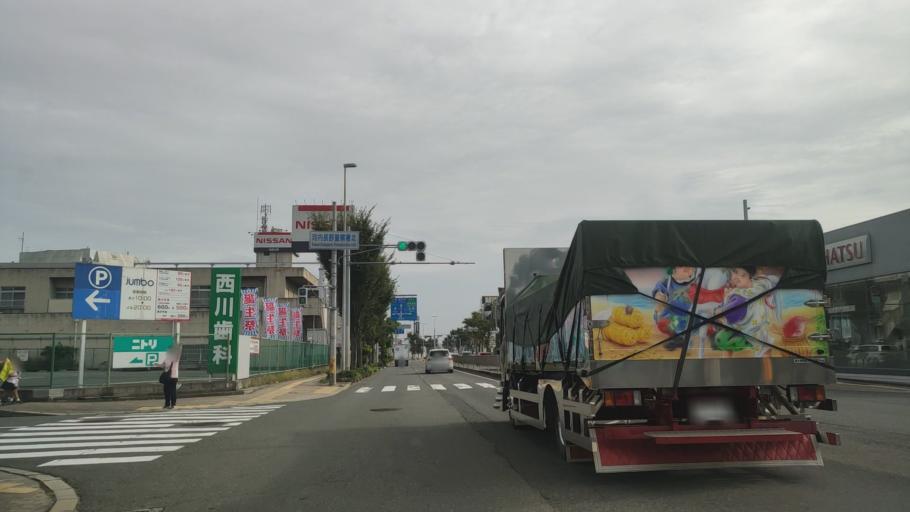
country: JP
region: Osaka
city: Tondabayashicho
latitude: 34.4555
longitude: 135.5634
